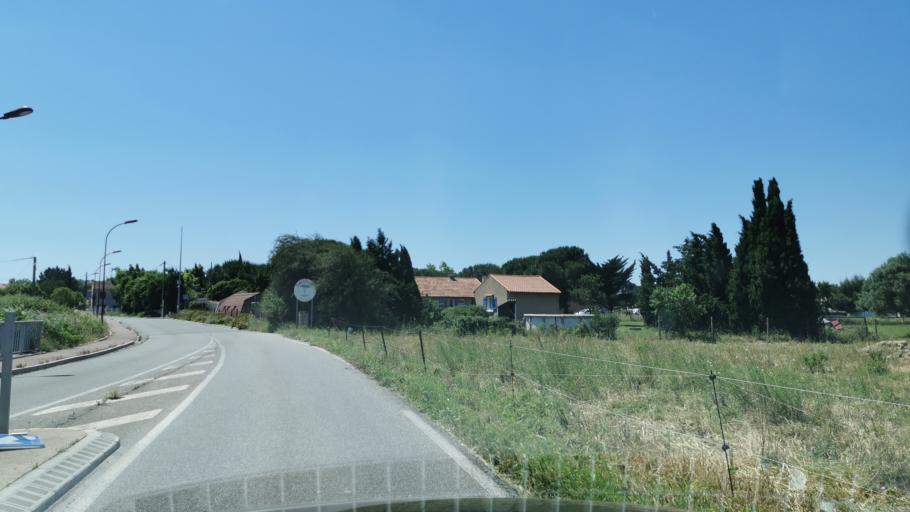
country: FR
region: Languedoc-Roussillon
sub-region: Departement de l'Aude
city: Saint-Marcel-sur-Aude
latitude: 43.2662
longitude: 2.9484
